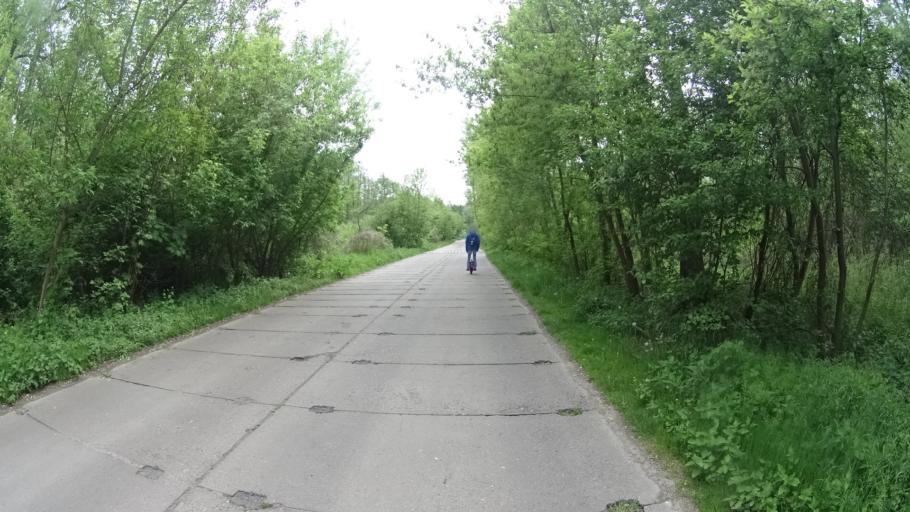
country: PL
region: Masovian Voivodeship
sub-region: Warszawa
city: Bemowo
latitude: 52.2821
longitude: 20.8863
